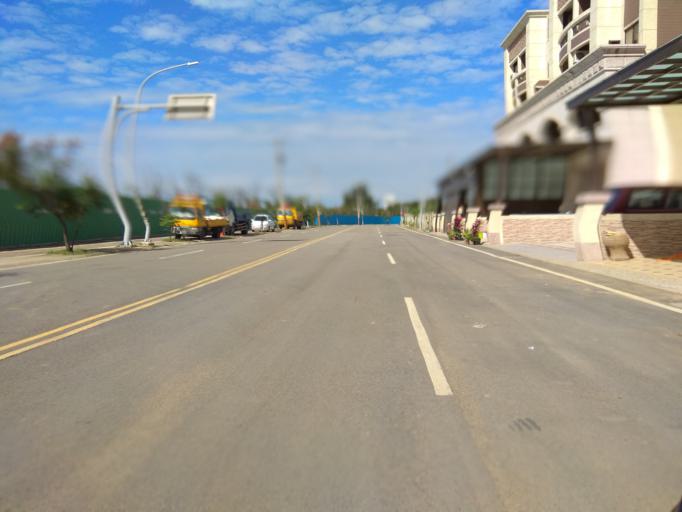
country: TW
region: Taiwan
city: Taoyuan City
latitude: 25.0419
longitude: 121.1344
